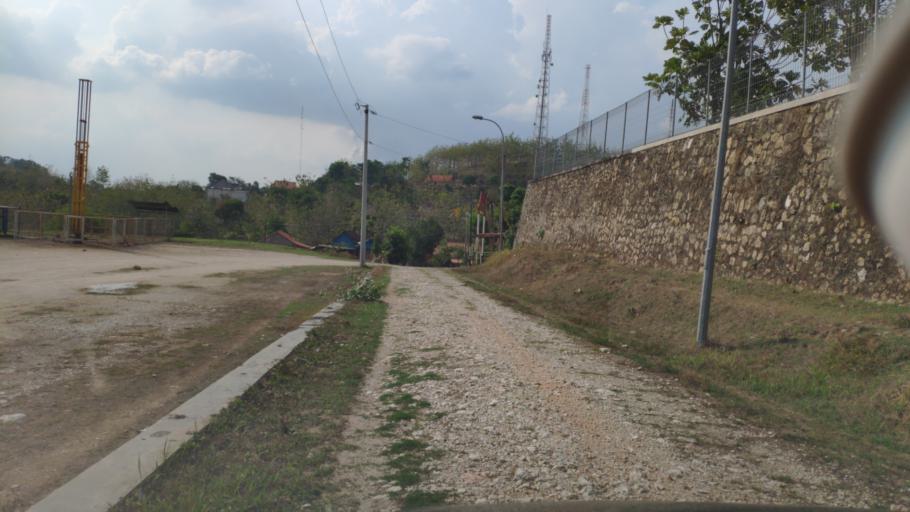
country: ID
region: Central Java
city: Semanggi
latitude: -7.0604
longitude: 111.4313
